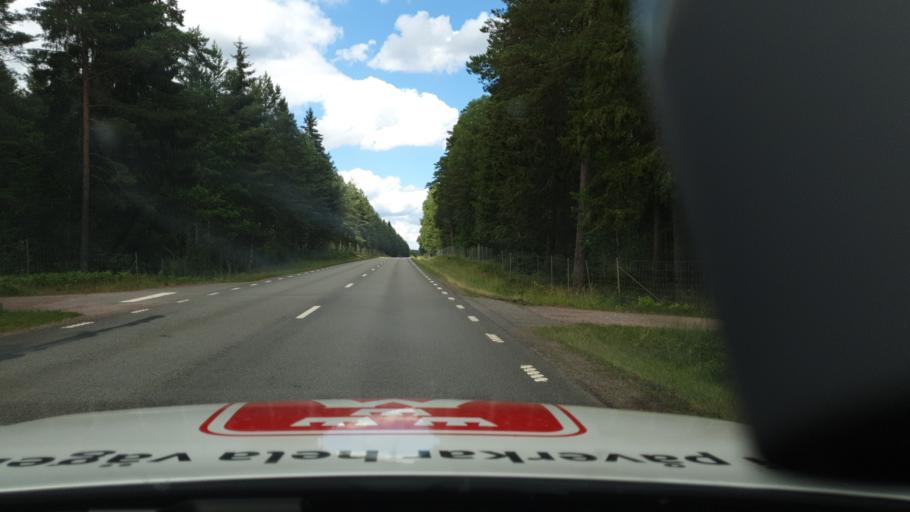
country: SE
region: Vaestra Goetaland
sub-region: Hjo Kommun
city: Hjo
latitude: 58.3711
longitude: 14.3518
